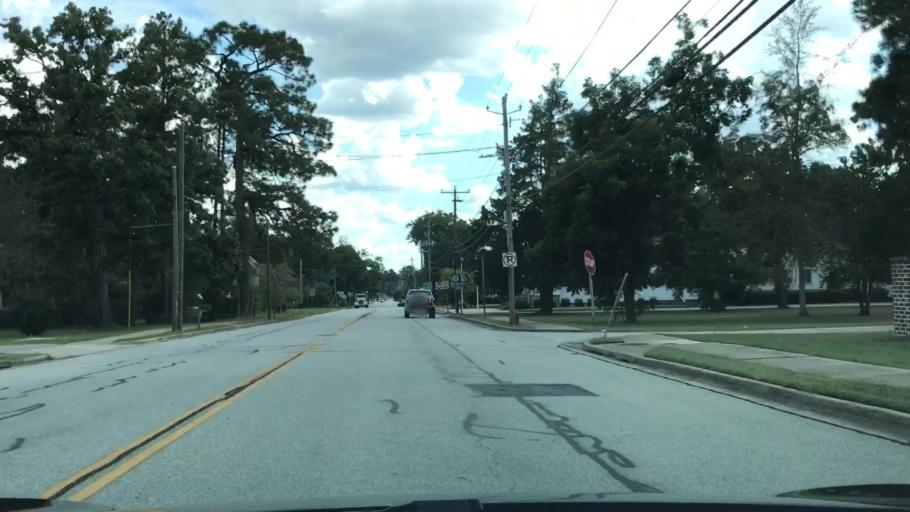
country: US
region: Georgia
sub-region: Jefferson County
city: Wadley
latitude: 32.8678
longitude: -82.4046
